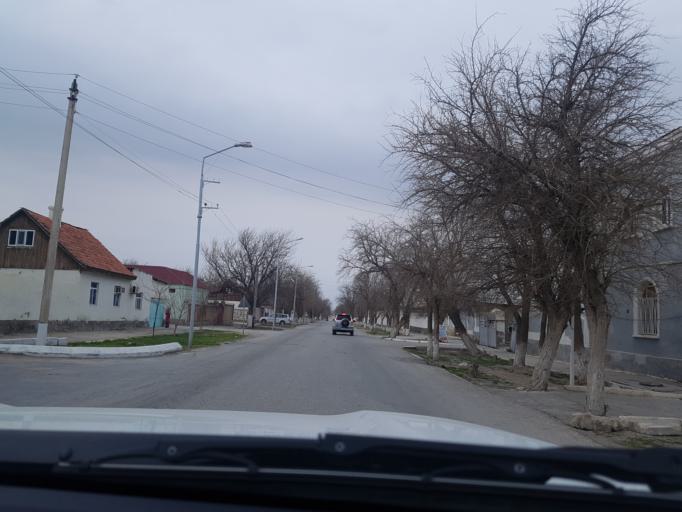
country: TM
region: Balkan
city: Balkanabat
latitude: 39.5067
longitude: 54.3747
